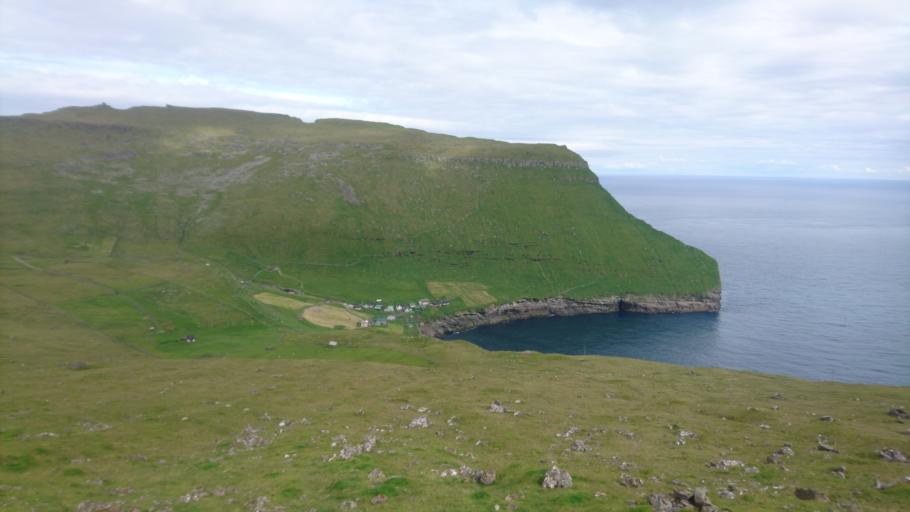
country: FO
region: Nordoyar
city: Klaksvik
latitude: 62.3251
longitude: -6.2873
